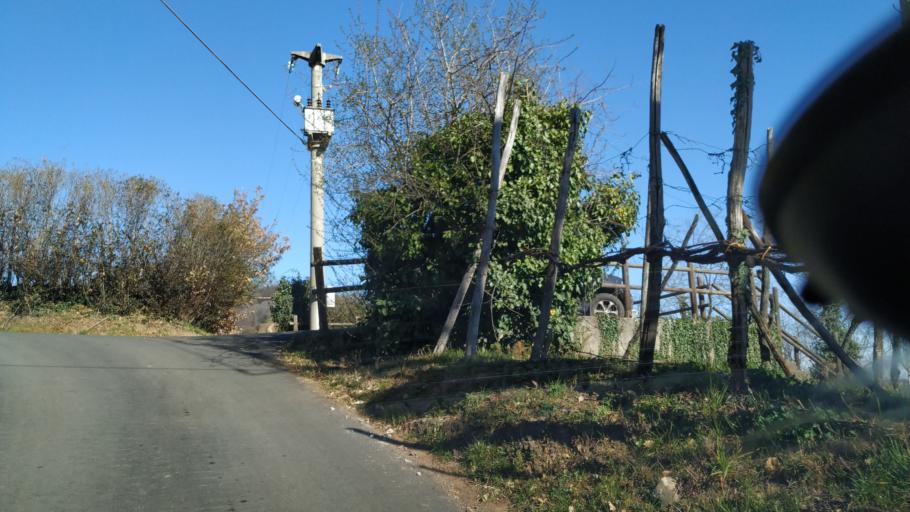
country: IT
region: Piedmont
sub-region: Provincia di Vercelli
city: Gattinara
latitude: 45.6222
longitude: 8.3662
